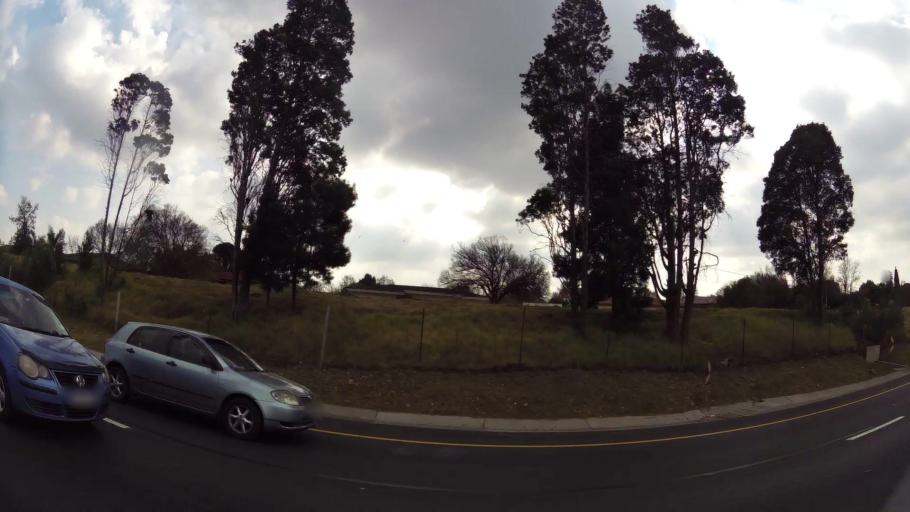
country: ZA
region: Gauteng
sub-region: Ekurhuleni Metropolitan Municipality
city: Benoni
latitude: -26.1808
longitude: 28.3026
